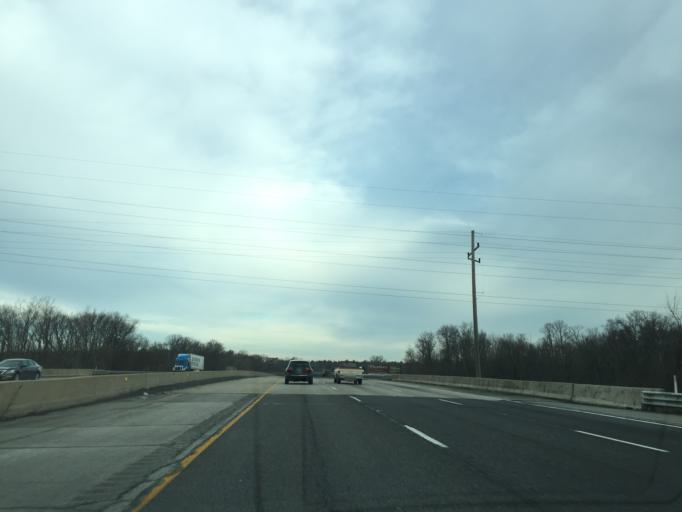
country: US
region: Indiana
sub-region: LaPorte County
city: Long Beach
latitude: 41.7180
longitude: -86.8057
